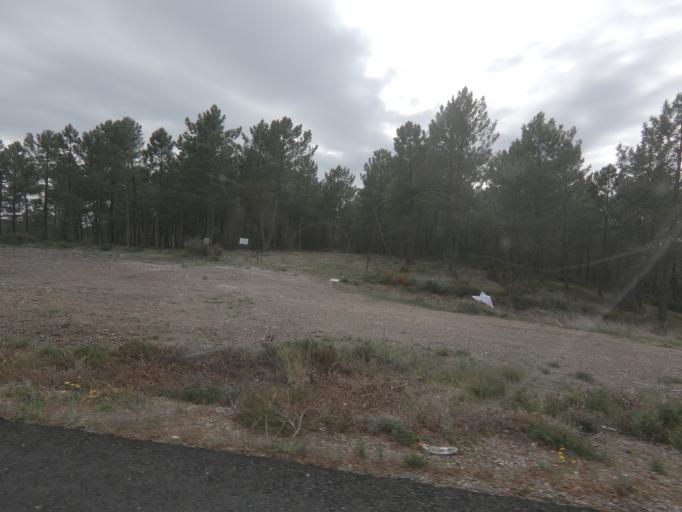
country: ES
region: Castille and Leon
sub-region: Provincia de Salamanca
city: Penaparda
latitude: 40.2618
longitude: -6.6893
